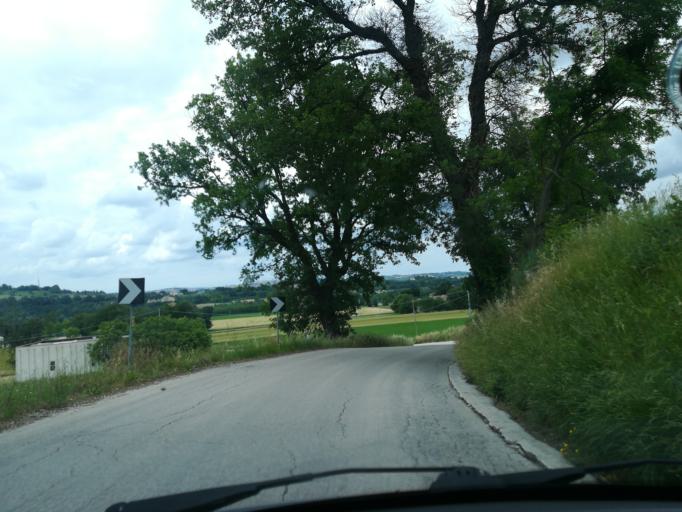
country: IT
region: The Marches
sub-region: Provincia di Macerata
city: Petriolo
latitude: 43.2293
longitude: 13.4619
